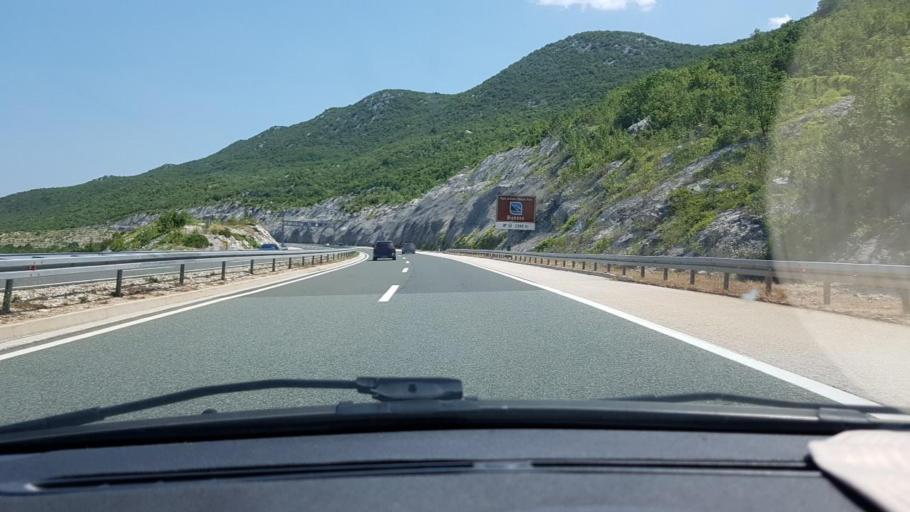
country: HR
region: Splitsko-Dalmatinska
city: Vrgorac
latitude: 43.2275
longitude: 17.2355
